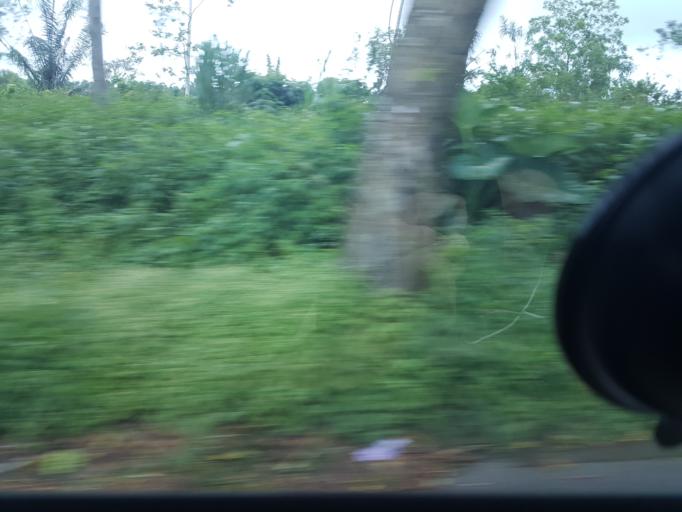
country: ID
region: Bali
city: Banjar Kedisan
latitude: -8.3009
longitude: 115.3549
